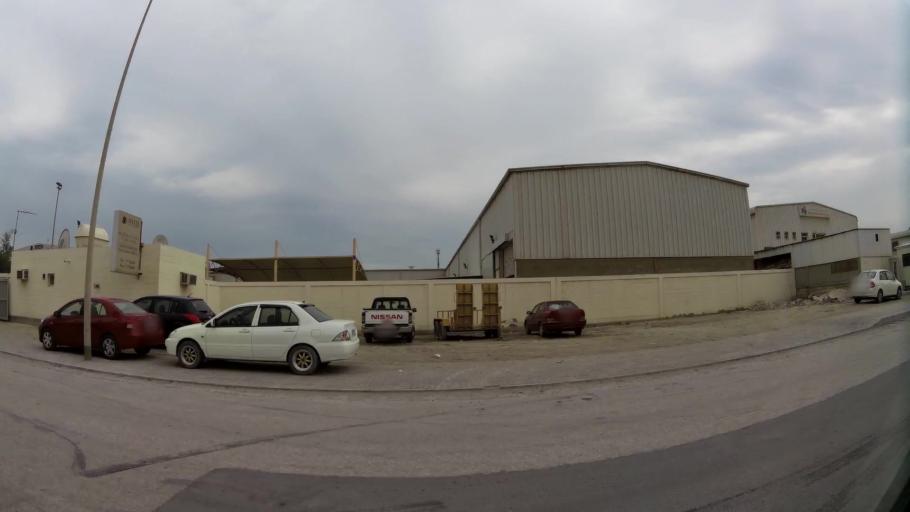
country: BH
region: Northern
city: Sitrah
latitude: 26.1814
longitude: 50.6155
